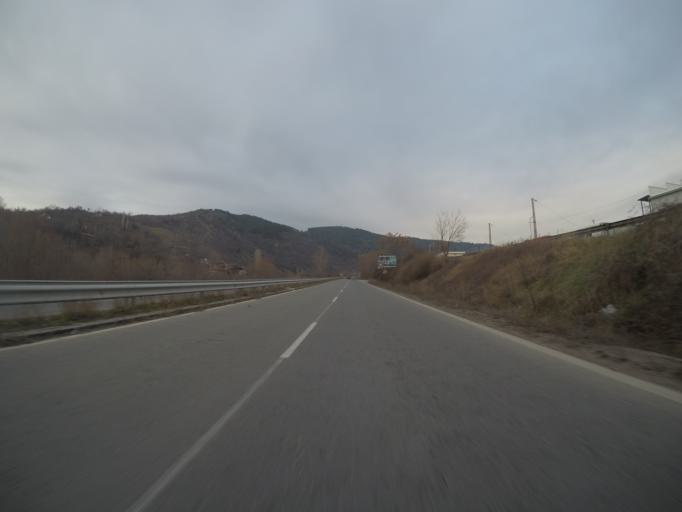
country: BG
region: Kyustendil
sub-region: Obshtina Dupnitsa
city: Dupnitsa
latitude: 42.2629
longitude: 23.1032
